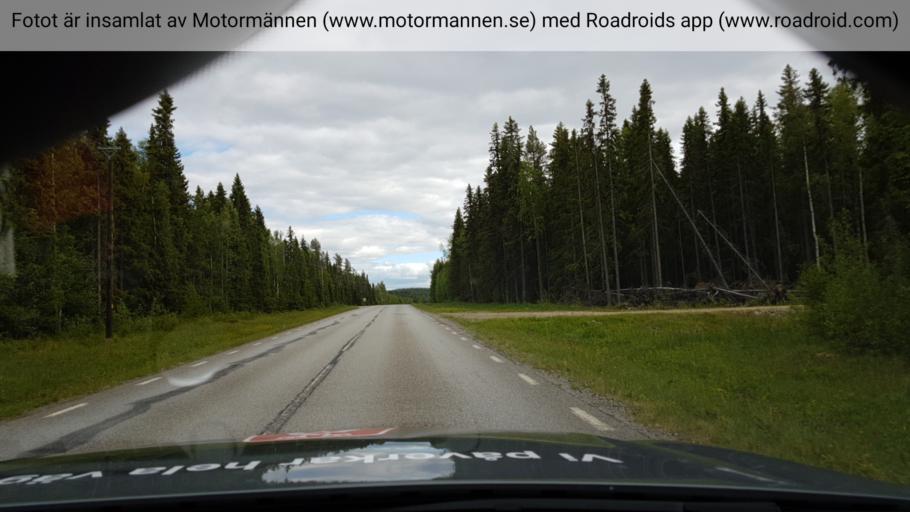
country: SE
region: Jaemtland
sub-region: Stroemsunds Kommun
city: Stroemsund
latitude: 63.9258
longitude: 15.5086
